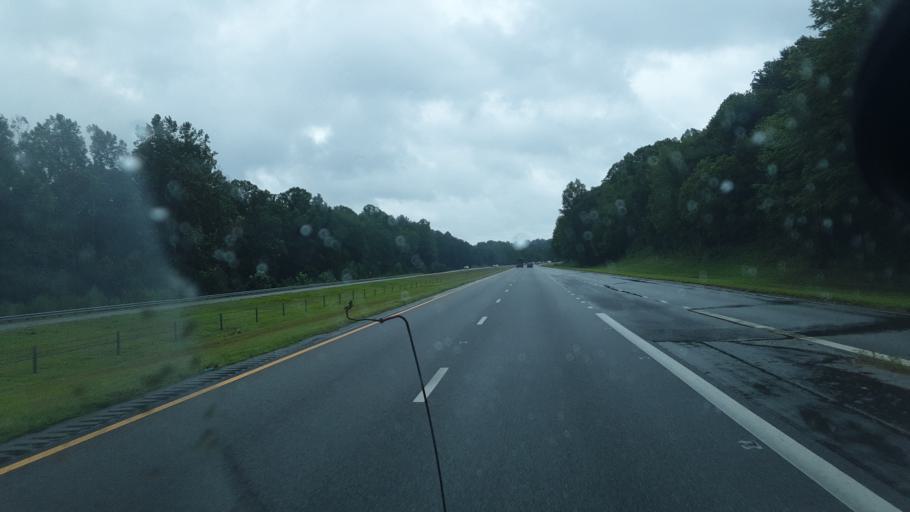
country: US
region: North Carolina
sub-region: Davidson County
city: Wallburg
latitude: 36.0377
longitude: -80.0994
